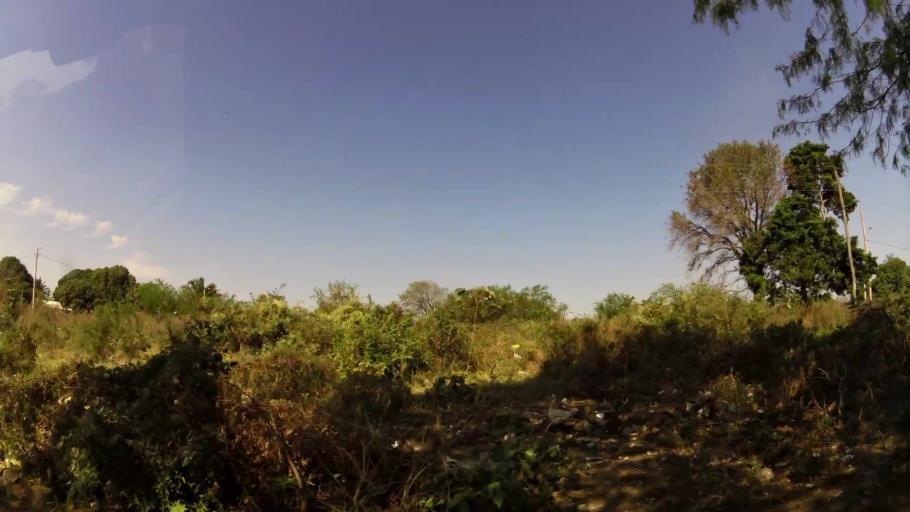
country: BO
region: Santa Cruz
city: Cotoca
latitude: -17.7146
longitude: -63.0644
